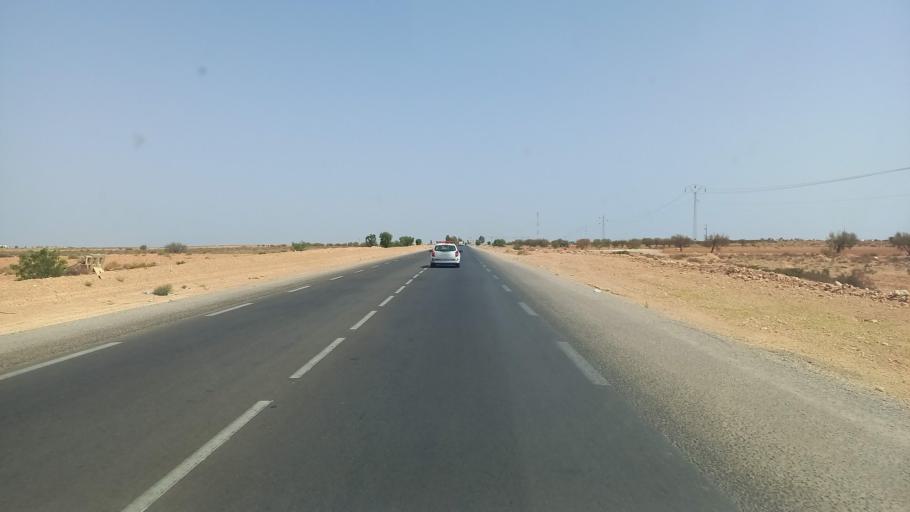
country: TN
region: Madanin
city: Medenine
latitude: 33.3787
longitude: 10.6977
